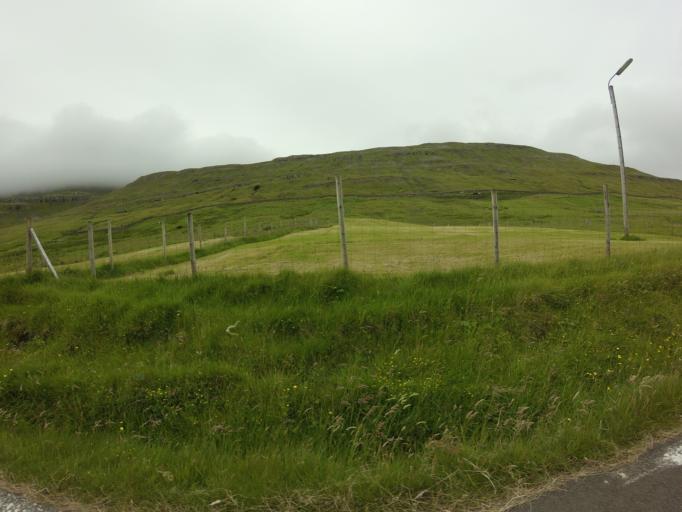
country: FO
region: Sandoy
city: Sandur
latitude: 61.8111
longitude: -6.6884
